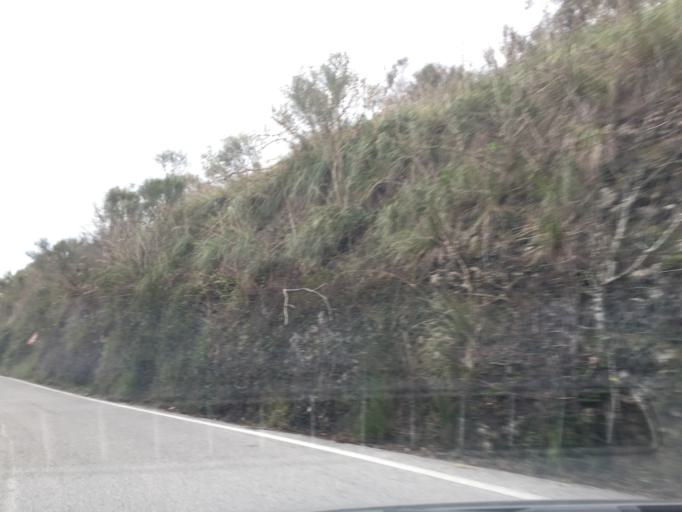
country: IT
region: Latium
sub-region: Provincia di Frosinone
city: Cassino
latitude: 41.4932
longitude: 13.8201
